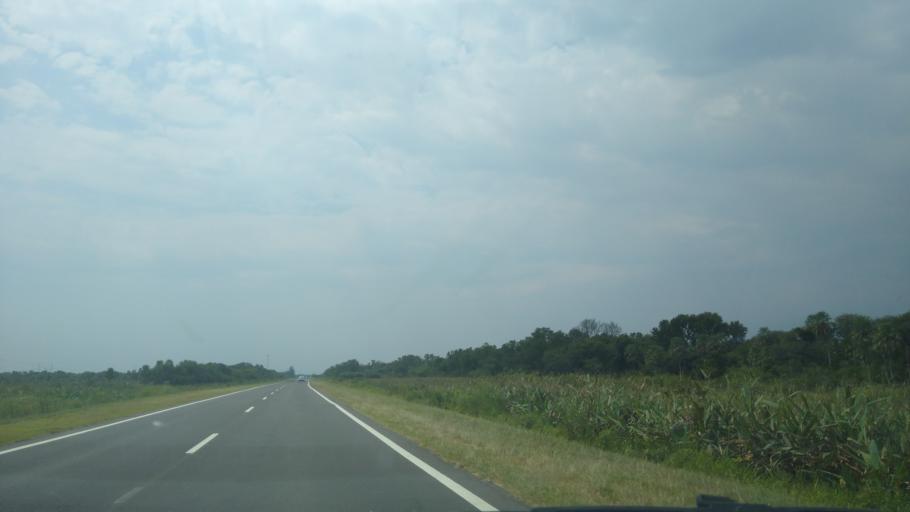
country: AR
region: Chaco
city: Margarita Belen
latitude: -27.1075
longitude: -58.9663
